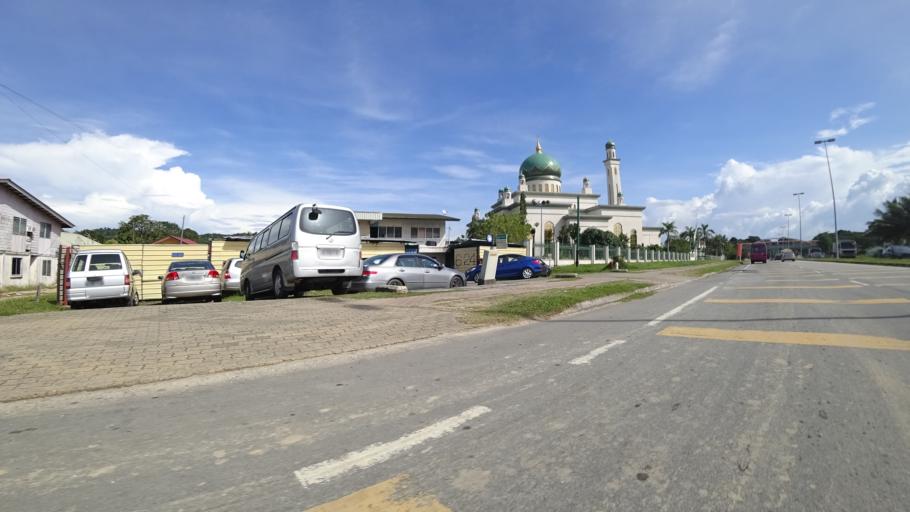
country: BN
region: Brunei and Muara
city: Bandar Seri Begawan
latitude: 4.9400
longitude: 114.8418
